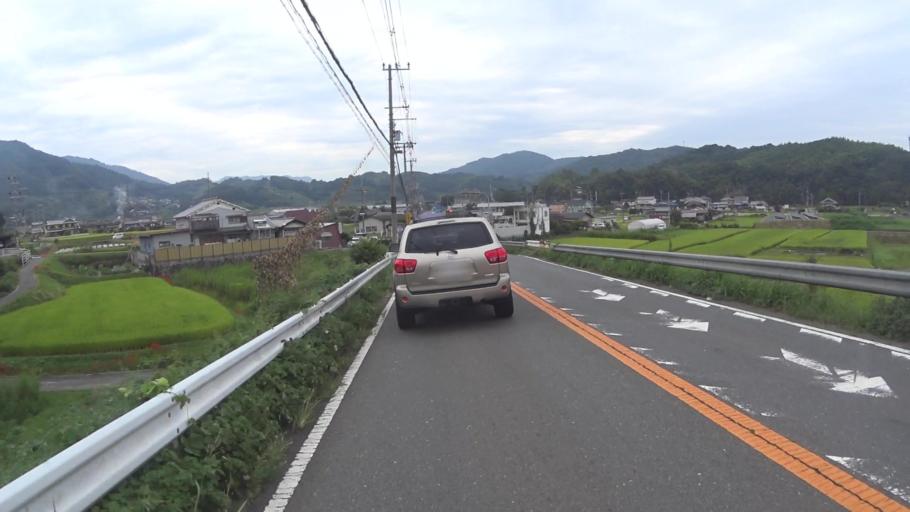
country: JP
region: Nara
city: Nara-shi
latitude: 34.7644
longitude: 135.8647
